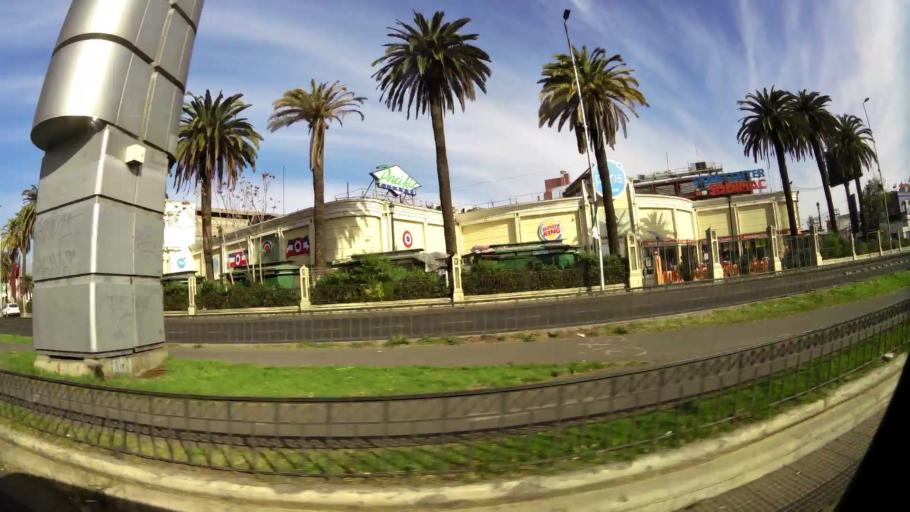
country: CL
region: Santiago Metropolitan
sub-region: Provincia de Santiago
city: Santiago
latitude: -33.4511
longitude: -70.6800
